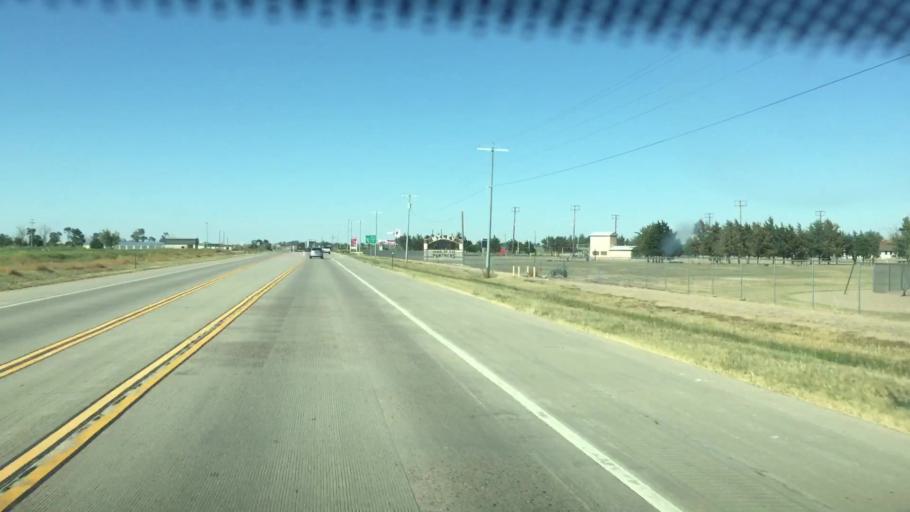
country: US
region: Colorado
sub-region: Prowers County
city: Lamar
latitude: 38.1545
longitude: -102.7237
